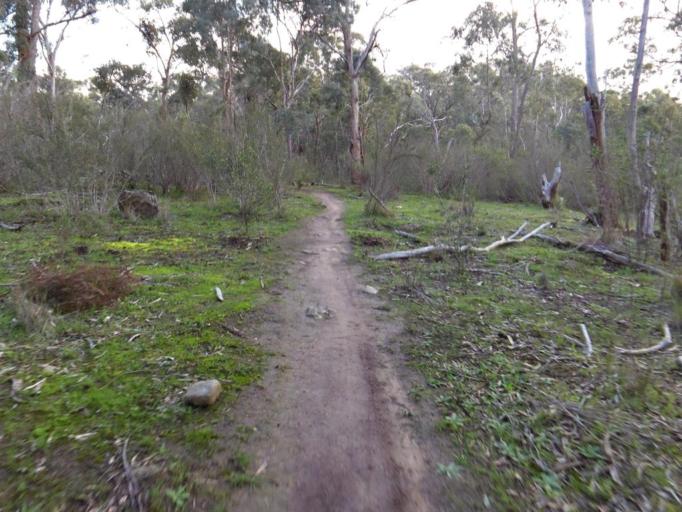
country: AU
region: Victoria
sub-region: Banyule
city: Watsonia North
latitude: -37.6816
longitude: 145.0945
